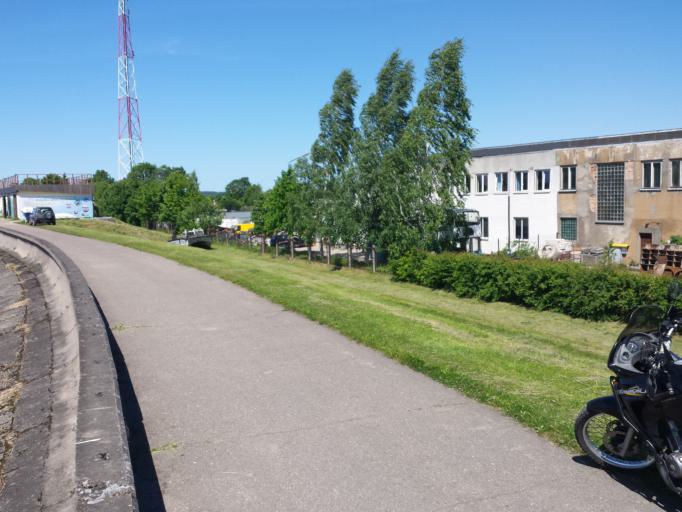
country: LV
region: Ikskile
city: Ikskile
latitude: 56.8291
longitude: 24.4852
